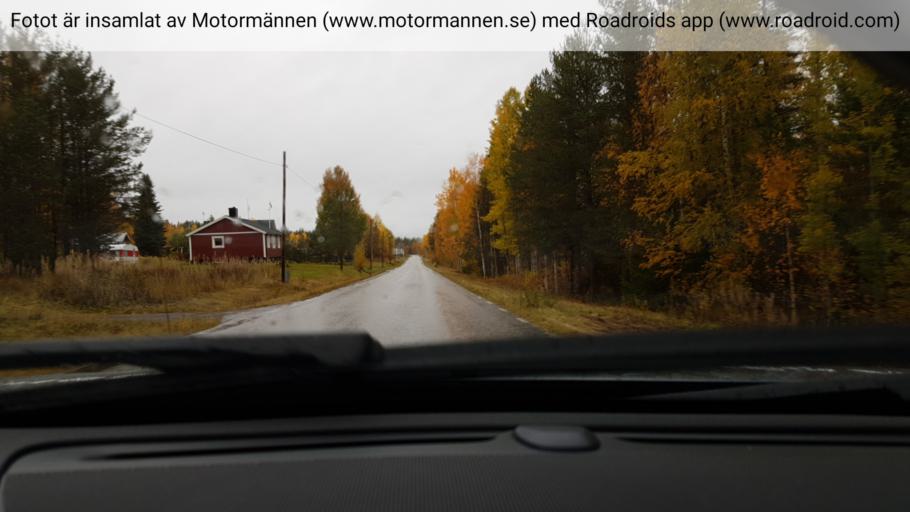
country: SE
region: Norrbotten
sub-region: Pajala Kommun
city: Pajala
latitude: 66.9148
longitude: 23.0214
